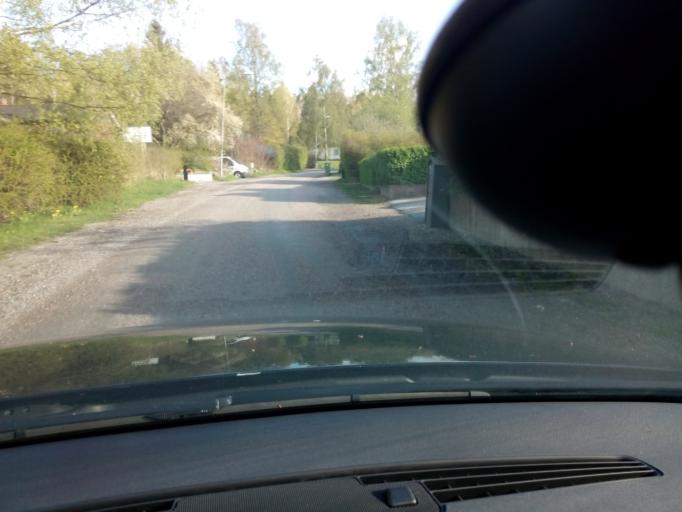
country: SE
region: Soedermanland
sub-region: Nykopings Kommun
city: Nykoping
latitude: 58.7774
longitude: 17.0895
